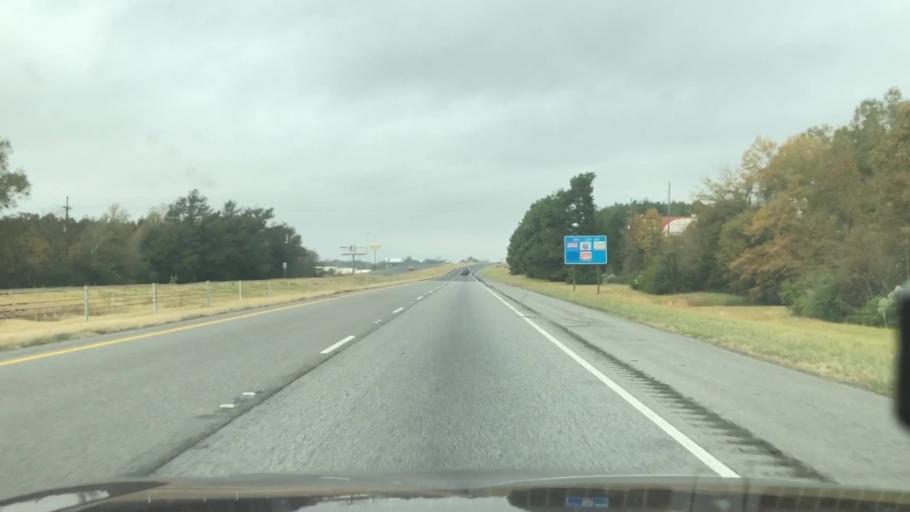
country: US
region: Louisiana
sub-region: Richland Parish
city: Rayville
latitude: 32.4567
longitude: -91.7515
